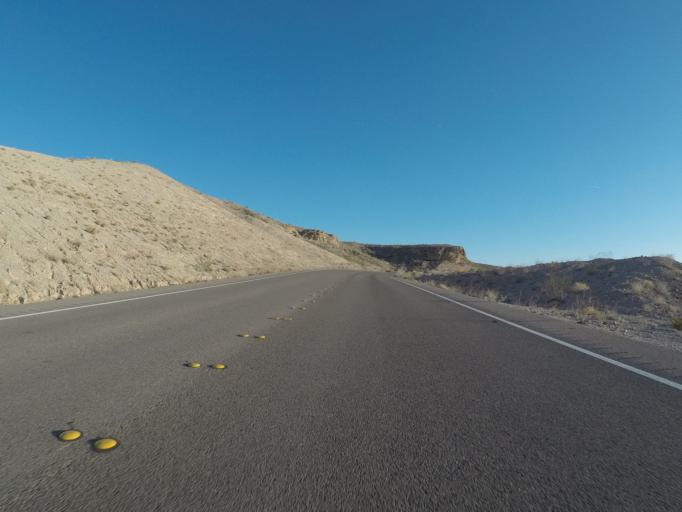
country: US
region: Nevada
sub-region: Clark County
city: Moapa Valley
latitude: 36.3036
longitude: -114.4896
